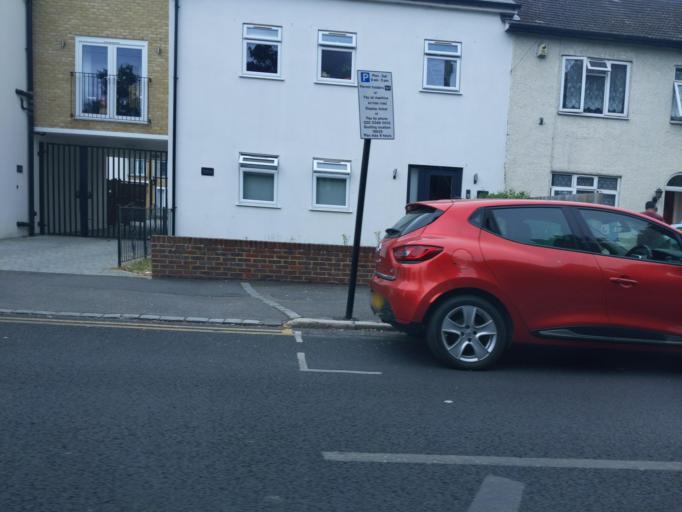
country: GB
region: England
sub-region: Greater London
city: Croydon
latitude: 51.3884
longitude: -0.1034
